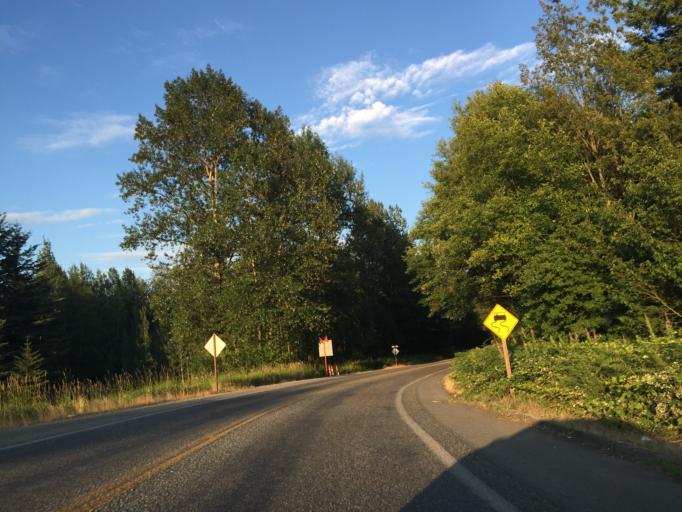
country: US
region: Washington
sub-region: Whatcom County
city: Birch Bay
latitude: 48.9360
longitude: -122.6596
